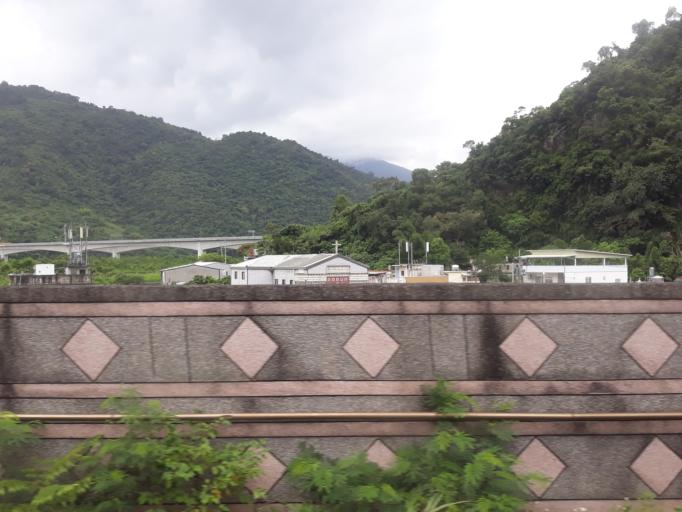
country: TW
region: Taiwan
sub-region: Yilan
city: Yilan
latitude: 24.4443
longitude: 121.7778
